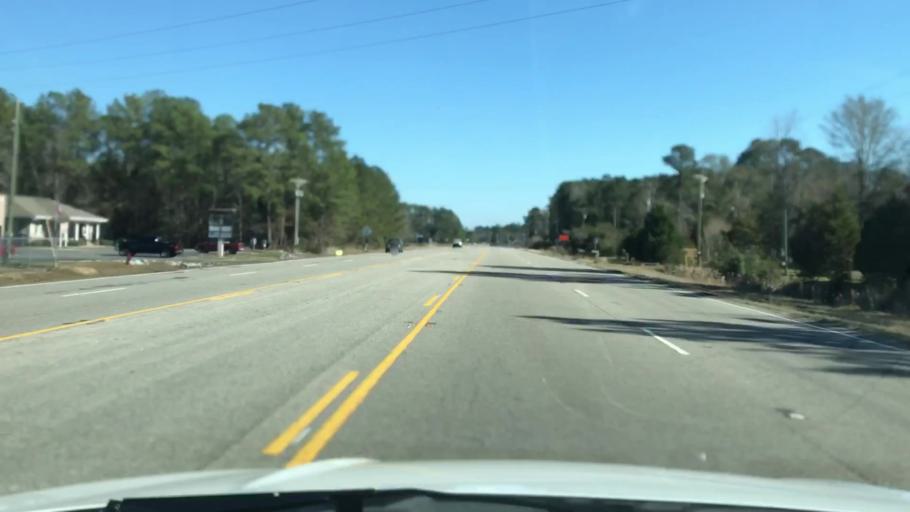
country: US
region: South Carolina
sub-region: Horry County
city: Garden City
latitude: 33.6297
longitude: -79.0314
